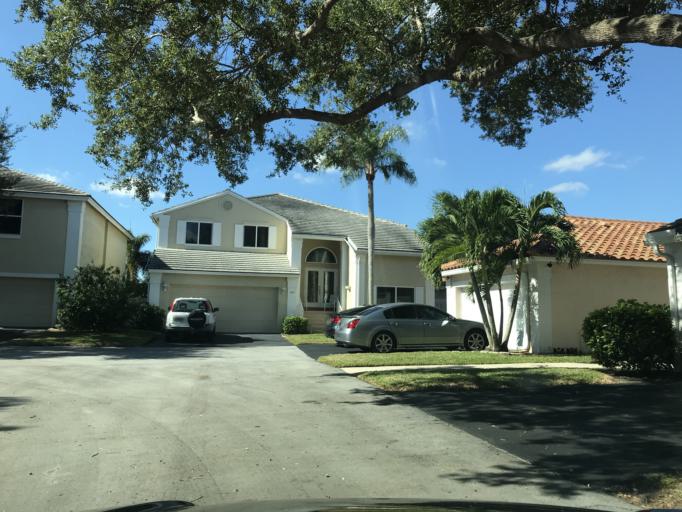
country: US
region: Florida
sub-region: Broward County
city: Pine Island Ridge
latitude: 26.1351
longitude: -80.2776
